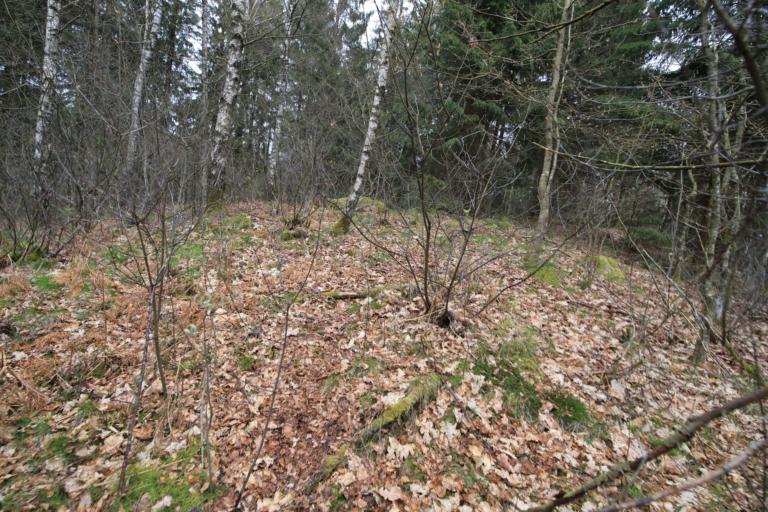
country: SE
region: Halland
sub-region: Varbergs Kommun
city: Tvaaker
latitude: 57.1500
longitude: 12.4562
